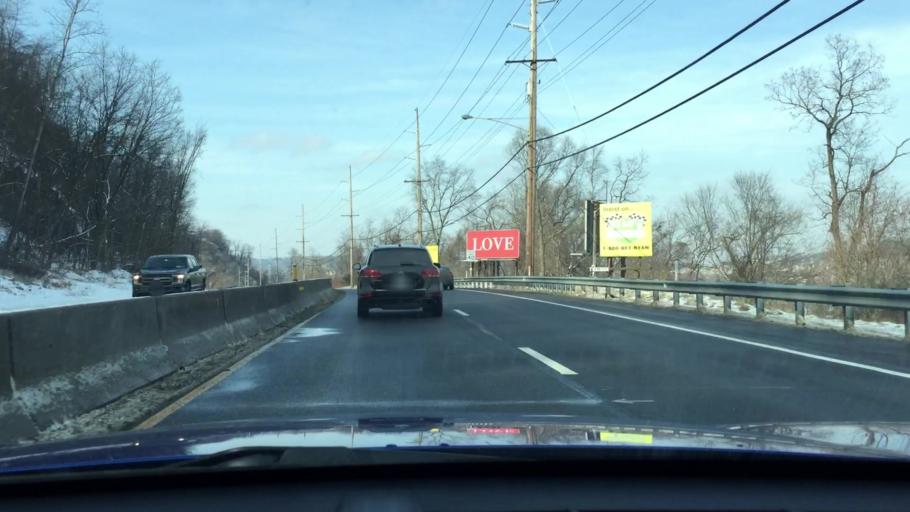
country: US
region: Pennsylvania
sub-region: Allegheny County
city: Braddock
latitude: 40.3979
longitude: -79.8759
